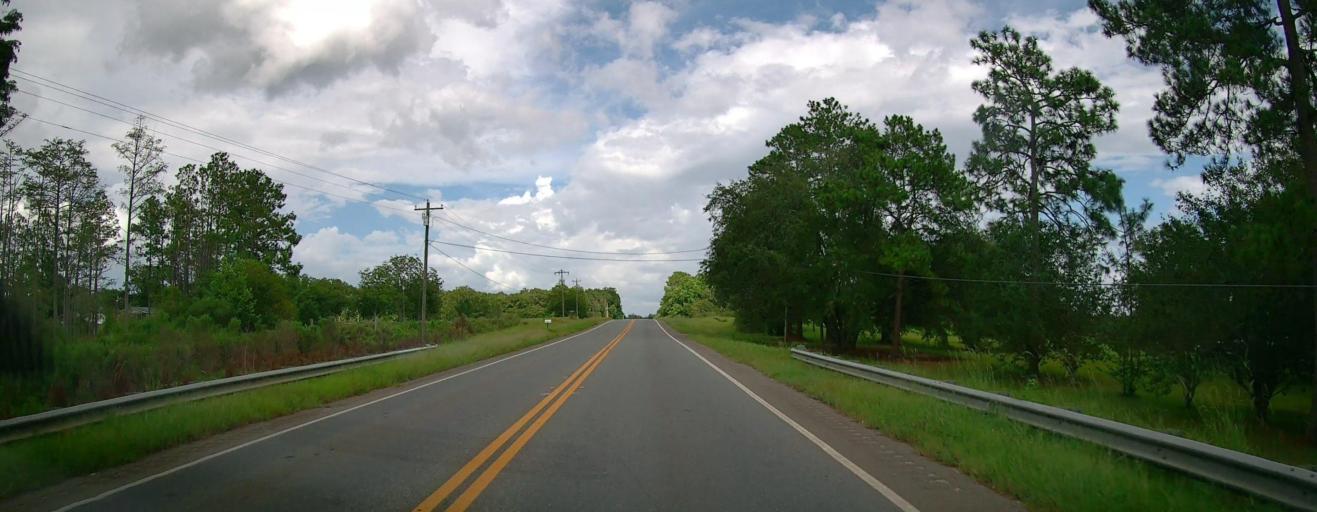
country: US
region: Georgia
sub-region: Coffee County
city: Douglas
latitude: 31.5390
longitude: -82.8833
